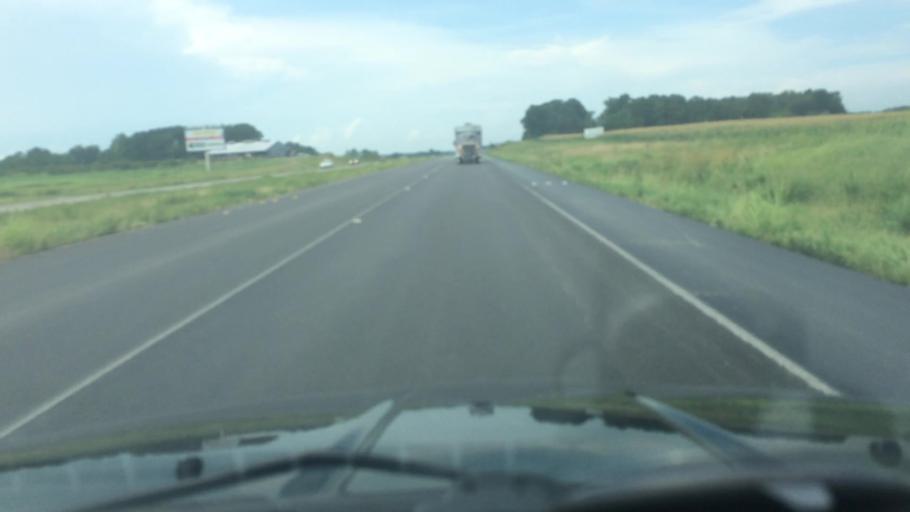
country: US
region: Missouri
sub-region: Saint Clair County
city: Osceola
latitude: 37.9775
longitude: -93.6483
